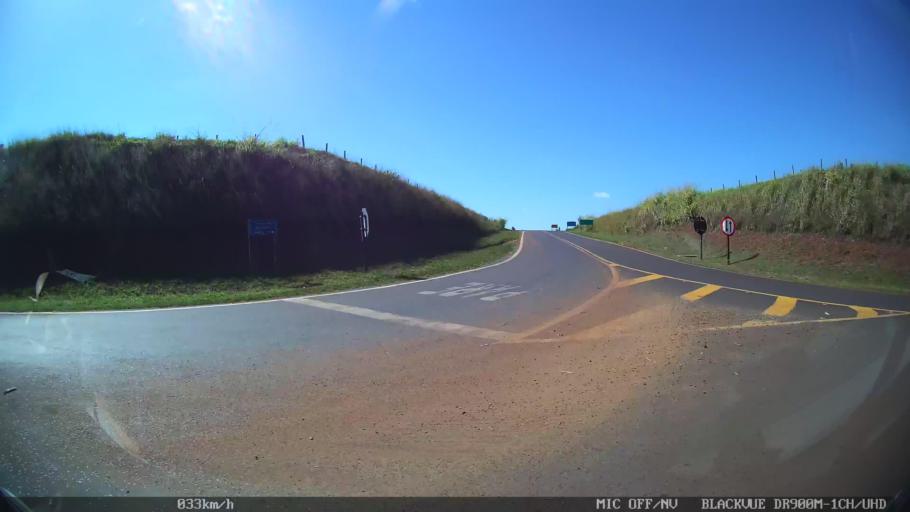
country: BR
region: Sao Paulo
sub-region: Franca
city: Franca
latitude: -20.6770
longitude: -47.4948
